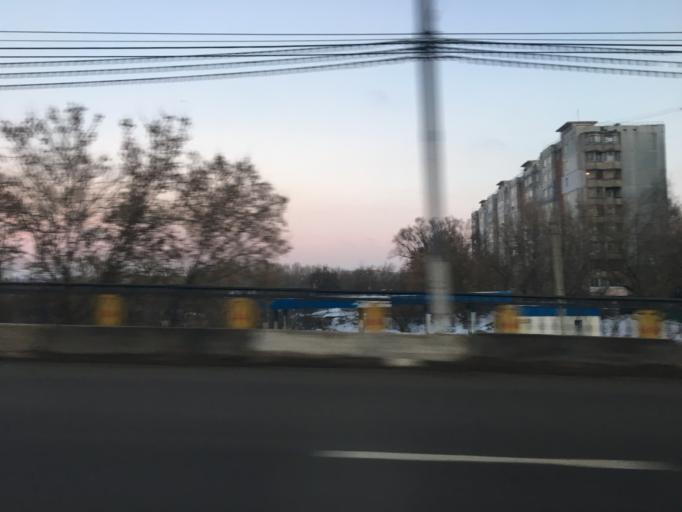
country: RU
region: Tula
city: Tula
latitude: 54.2206
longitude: 37.6261
